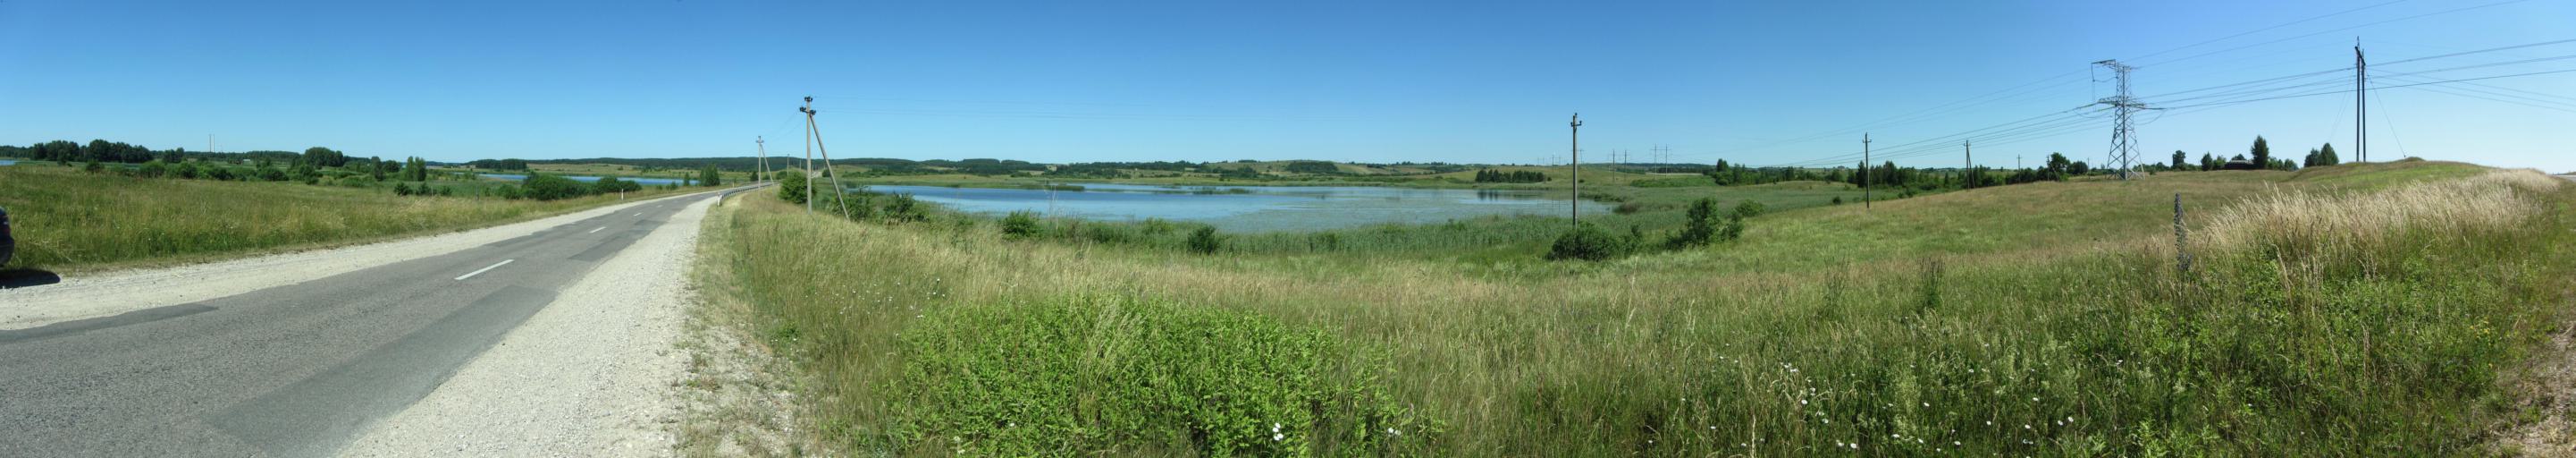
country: LT
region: Vilnius County
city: Elektrenai
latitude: 54.7200
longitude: 24.6760
